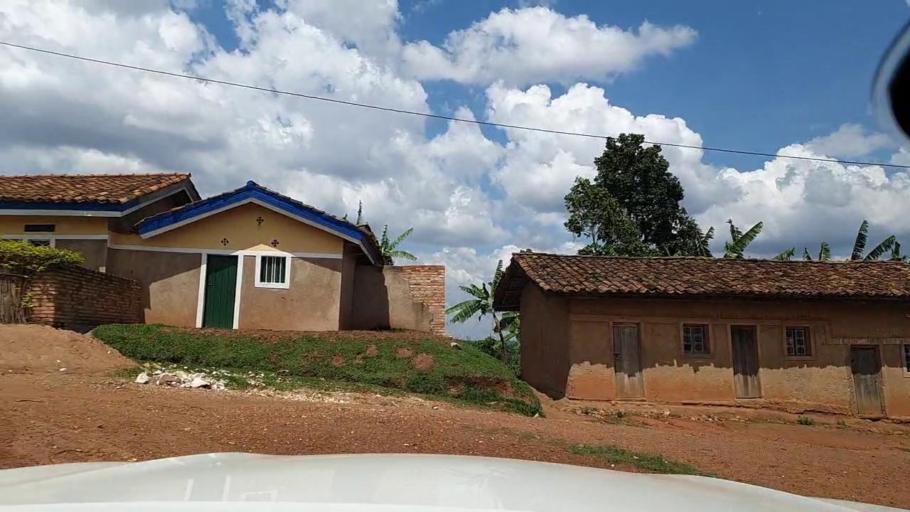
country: RW
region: Southern Province
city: Butare
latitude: -2.7473
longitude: 29.7062
